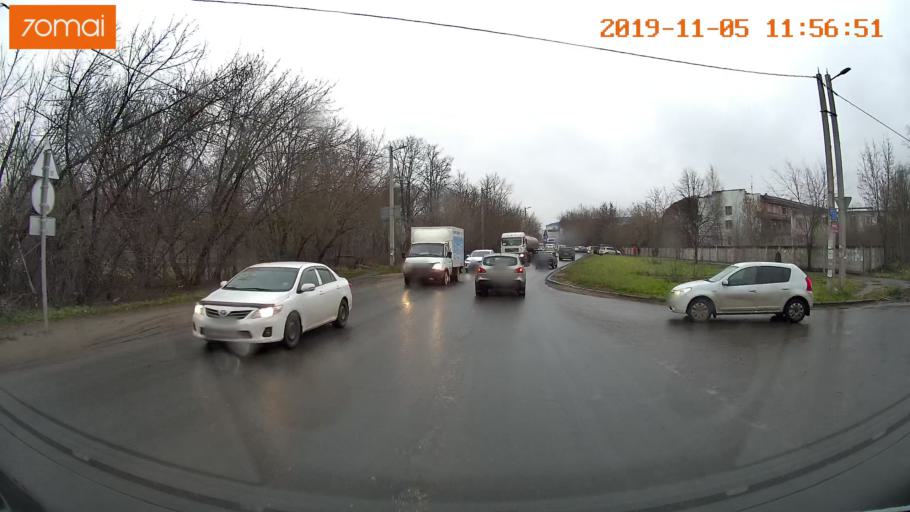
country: RU
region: Ivanovo
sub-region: Gorod Ivanovo
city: Ivanovo
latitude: 56.9854
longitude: 41.0327
